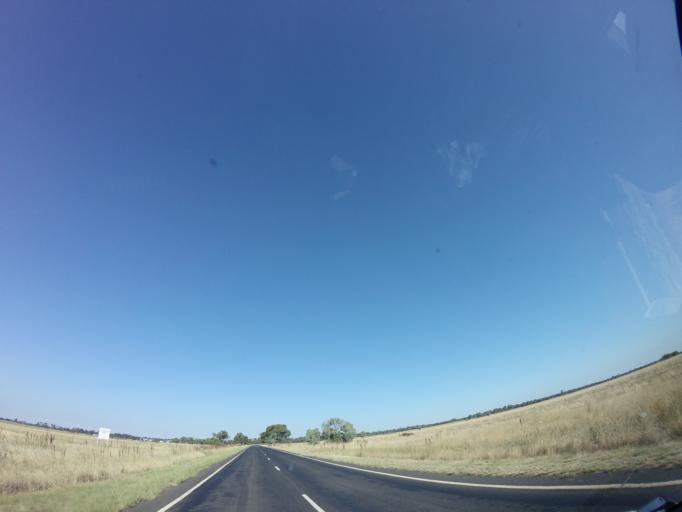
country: AU
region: New South Wales
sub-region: Gilgandra
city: Gilgandra
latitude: -31.7050
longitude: 148.6207
